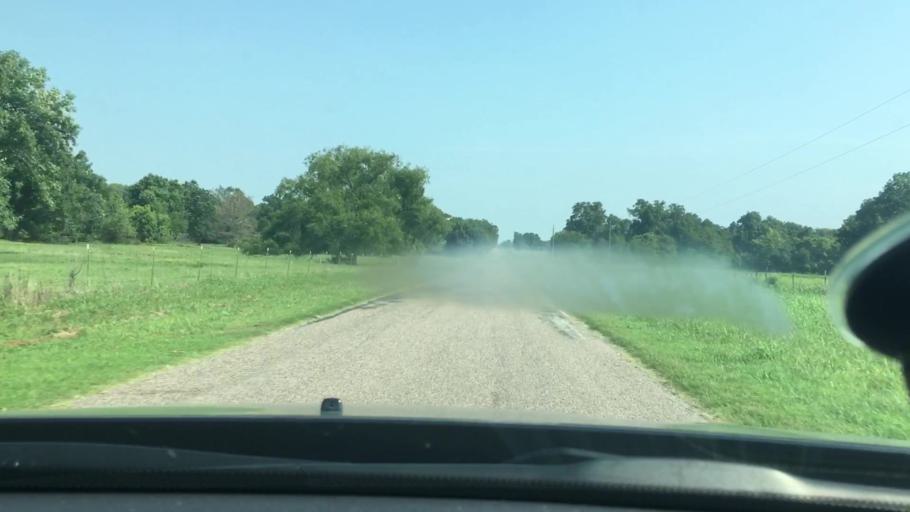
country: US
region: Oklahoma
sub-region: Pontotoc County
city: Ada
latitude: 34.6702
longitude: -96.5298
